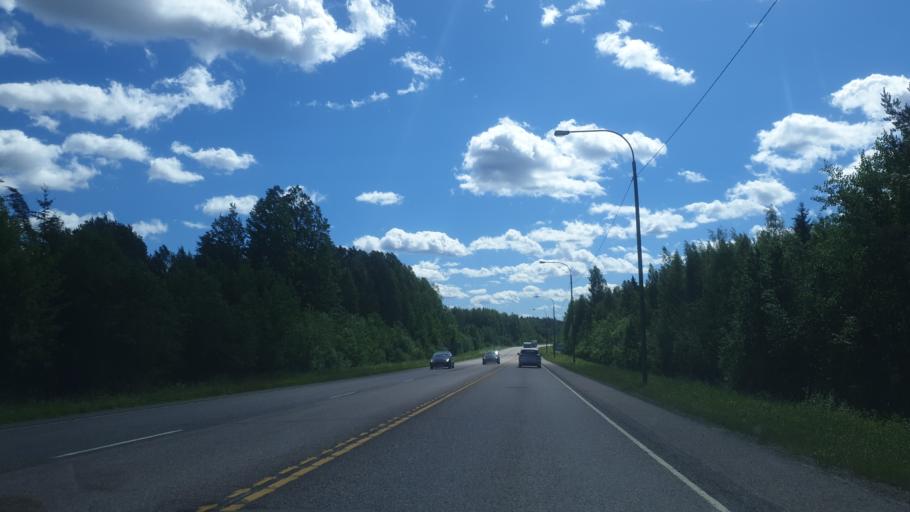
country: FI
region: Northern Savo
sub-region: Varkaus
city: Varkaus
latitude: 62.3570
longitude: 27.8130
